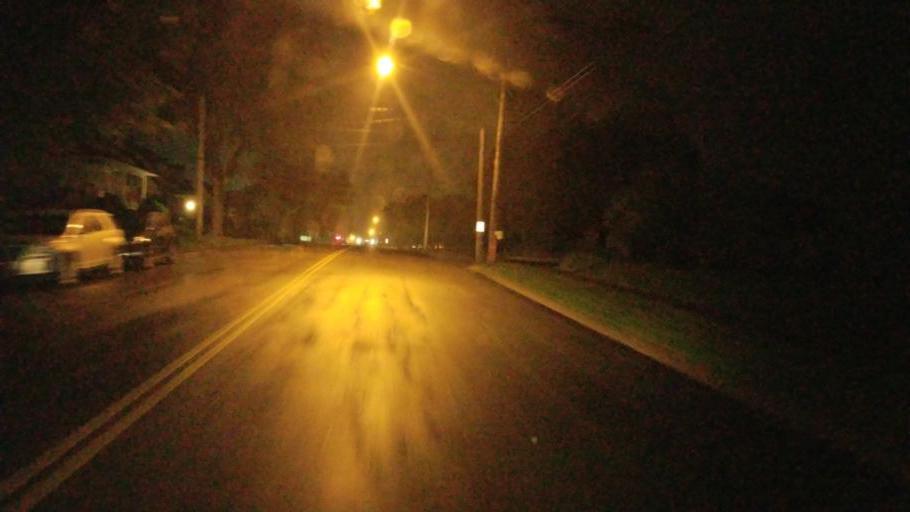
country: US
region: Ohio
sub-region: Highland County
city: Greenfield
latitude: 39.3575
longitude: -83.3851
